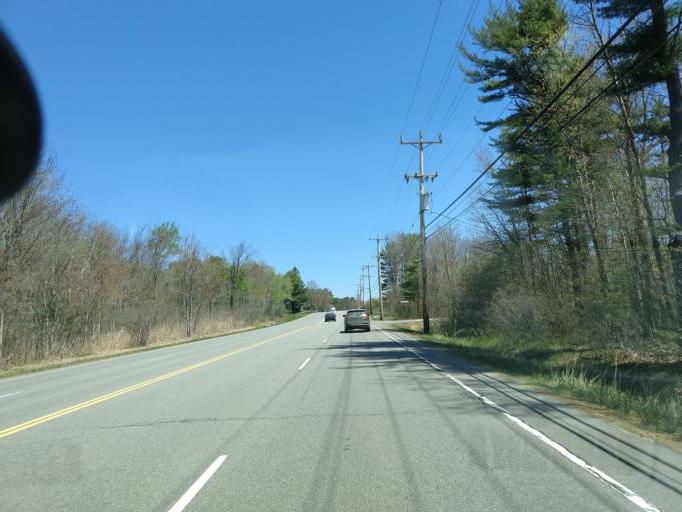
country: US
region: Maine
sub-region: York County
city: York Harbor
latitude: 43.1614
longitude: -70.6484
